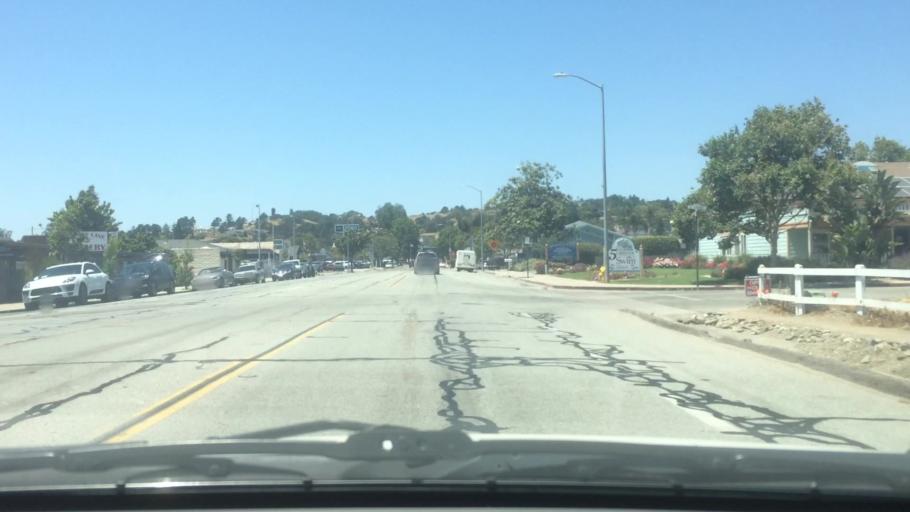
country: US
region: California
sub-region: San Luis Obispo County
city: Arroyo Grande
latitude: 35.1183
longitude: -120.5753
